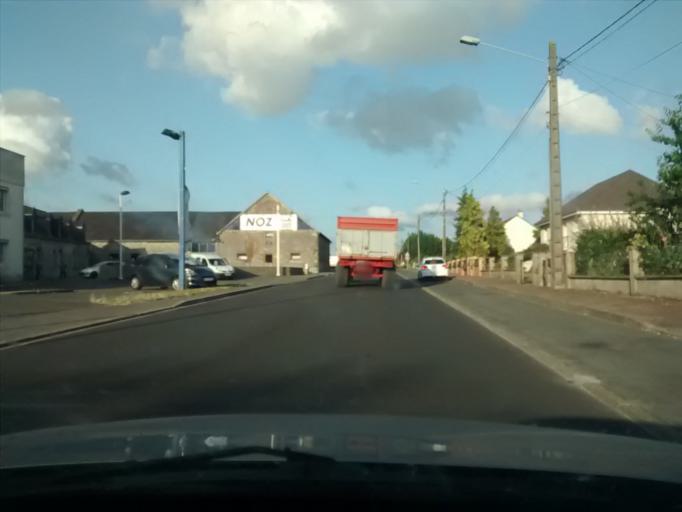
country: FR
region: Pays de la Loire
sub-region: Departement de la Mayenne
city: Evron
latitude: 48.1563
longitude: -0.3922
